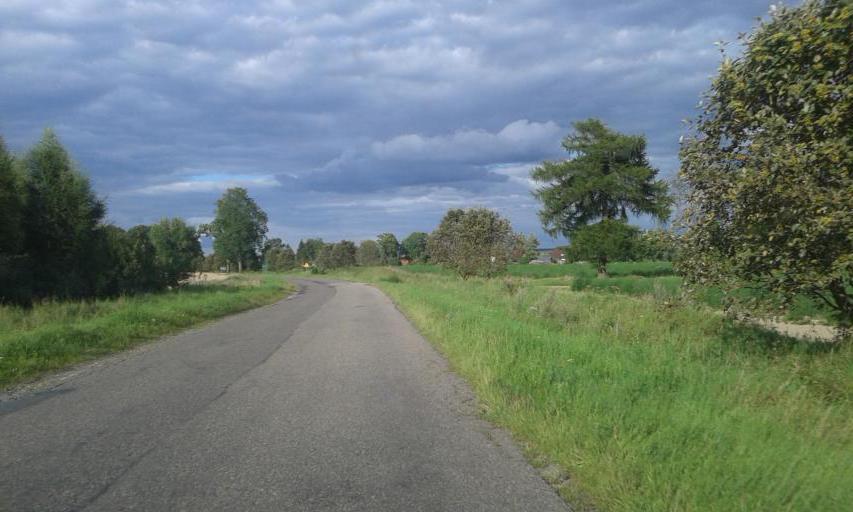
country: PL
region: West Pomeranian Voivodeship
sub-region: Powiat bialogardzki
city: Tychowo
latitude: 53.9054
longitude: 16.2395
